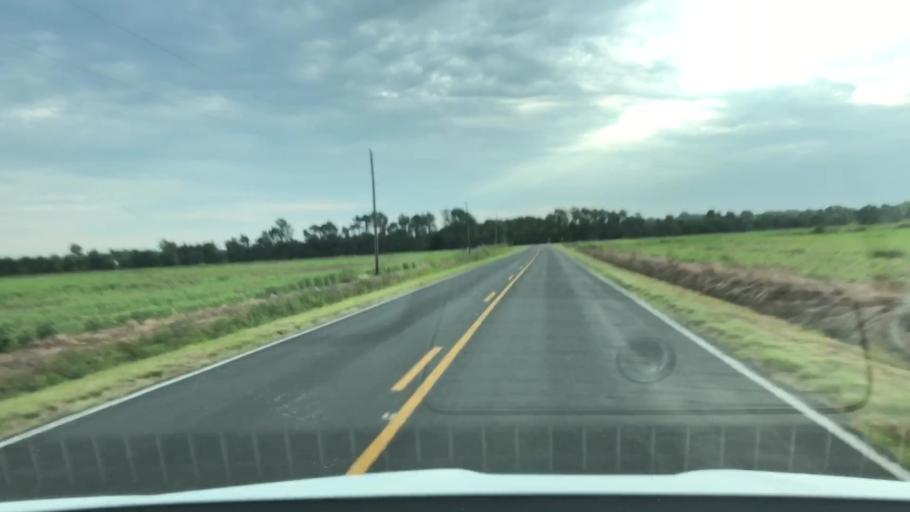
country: US
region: North Carolina
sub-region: Jones County
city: Trenton
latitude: 34.9993
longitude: -77.2759
